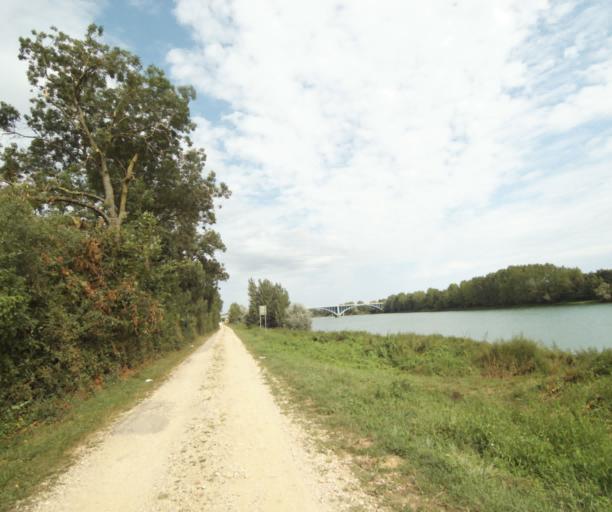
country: FR
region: Bourgogne
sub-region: Departement de Saone-et-Loire
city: Tournus
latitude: 46.5518
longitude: 4.9197
